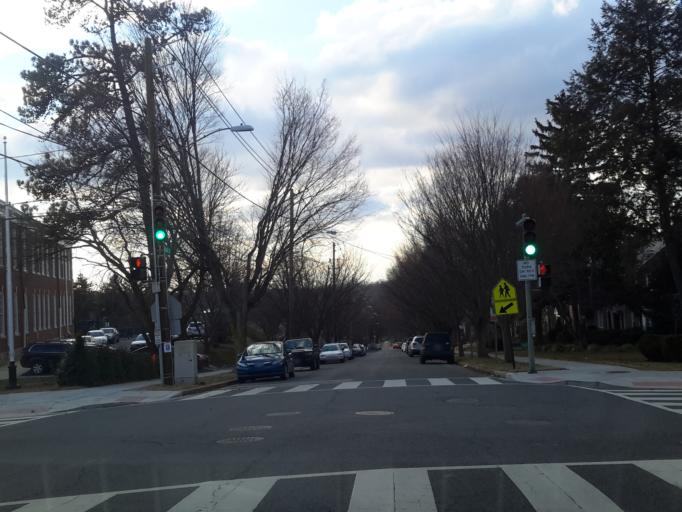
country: US
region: Maryland
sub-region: Montgomery County
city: Silver Spring
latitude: 38.9851
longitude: -77.0333
